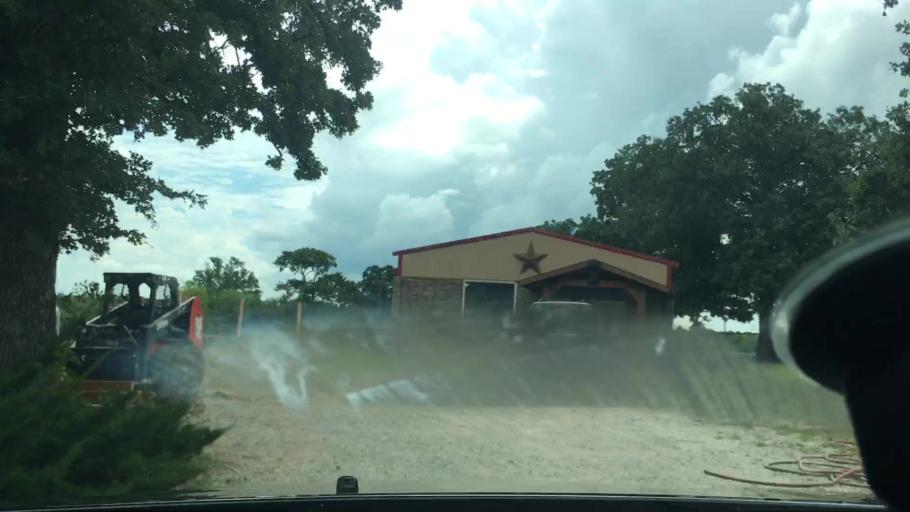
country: US
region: Oklahoma
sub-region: Carter County
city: Lone Grove
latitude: 34.2155
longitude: -97.2536
